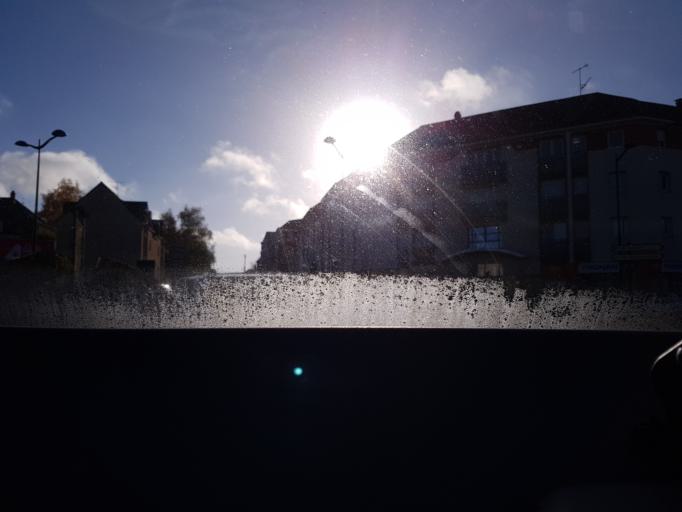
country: FR
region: Pays de la Loire
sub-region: Departement de la Mayenne
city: Mayenne
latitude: 48.3026
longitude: -0.6113
